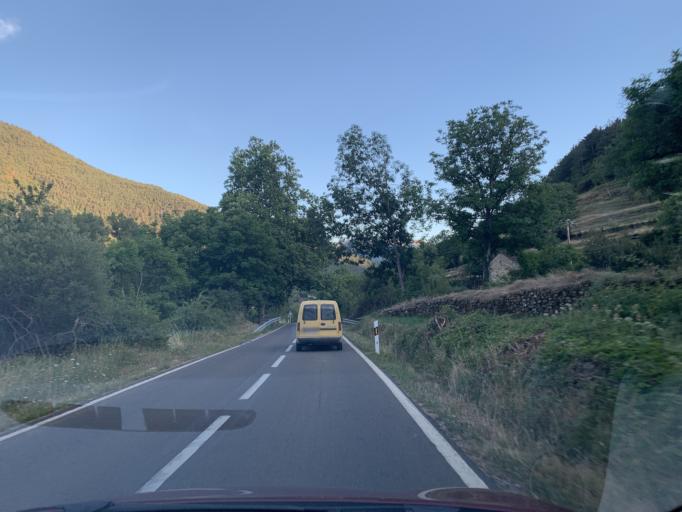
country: ES
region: Aragon
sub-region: Provincia de Huesca
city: Broto
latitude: 42.6109
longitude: -0.1243
